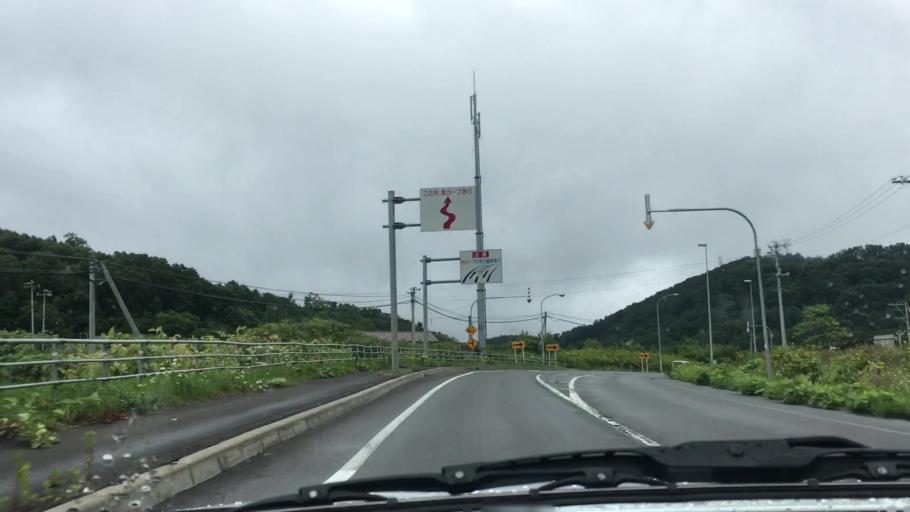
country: JP
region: Hokkaido
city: Niseko Town
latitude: 42.6079
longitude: 140.7286
